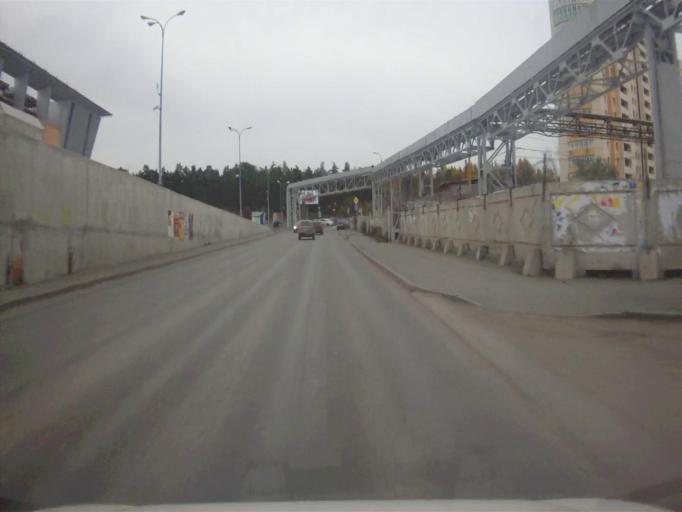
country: RU
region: Chelyabinsk
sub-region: Gorod Chelyabinsk
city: Chelyabinsk
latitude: 55.1704
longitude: 61.3540
